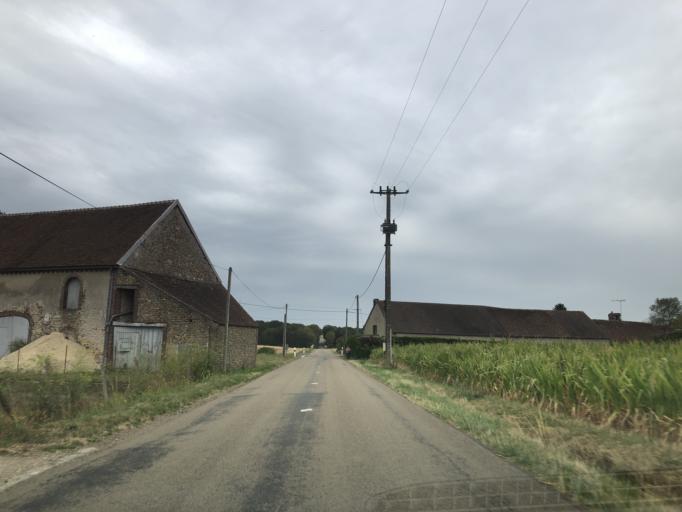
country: FR
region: Centre
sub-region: Departement du Loiret
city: Douchy
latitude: 47.9745
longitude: 3.1431
